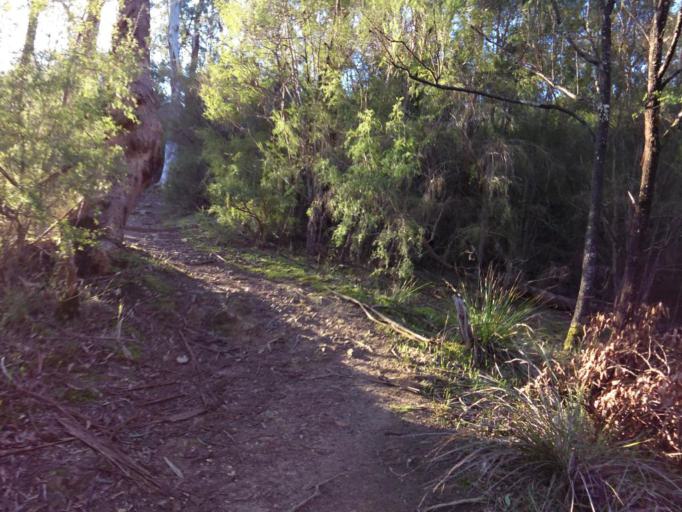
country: AU
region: Victoria
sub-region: Manningham
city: Warrandyte
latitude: -37.7279
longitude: 145.2425
